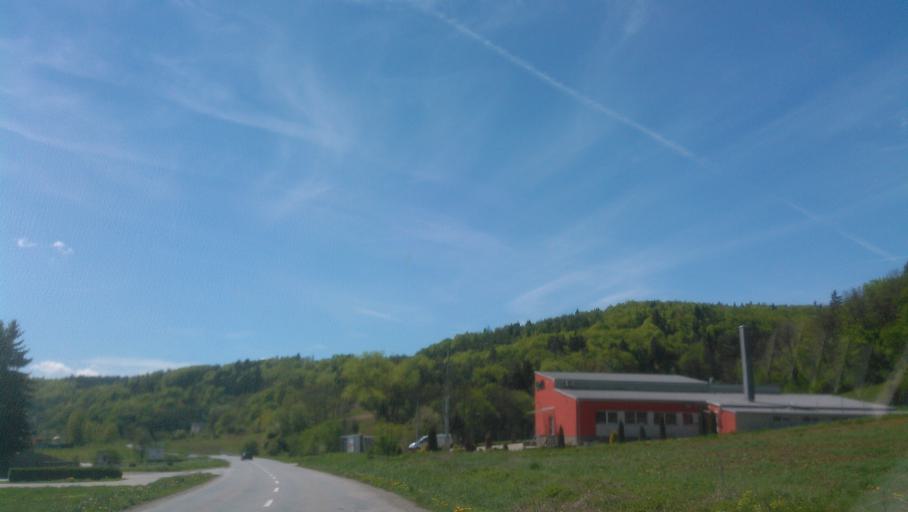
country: SK
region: Banskobystricky
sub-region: Okres Banska Bystrica
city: Banska Bystrica
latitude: 48.7582
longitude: 19.2504
